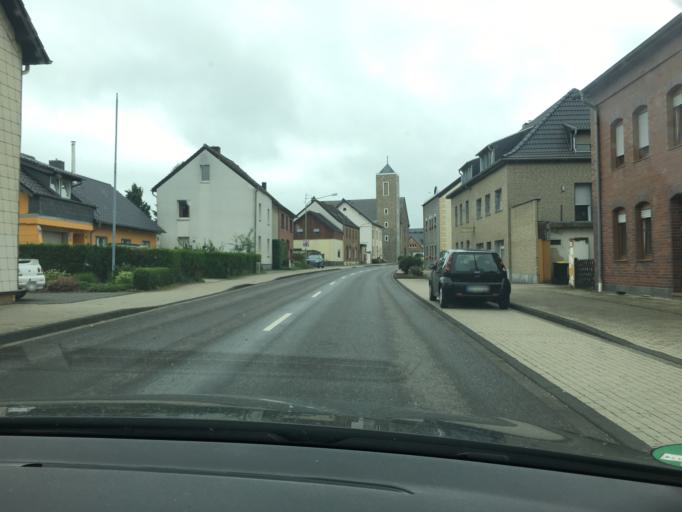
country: DE
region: North Rhine-Westphalia
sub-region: Regierungsbezirk Koln
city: Hurtgenwald
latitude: 50.7117
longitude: 6.3809
